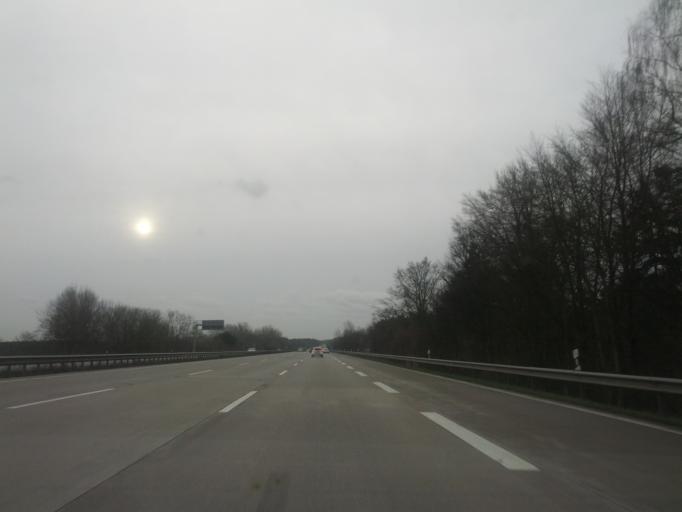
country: DE
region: Lower Saxony
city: Brackel
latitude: 53.3047
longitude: 10.0725
